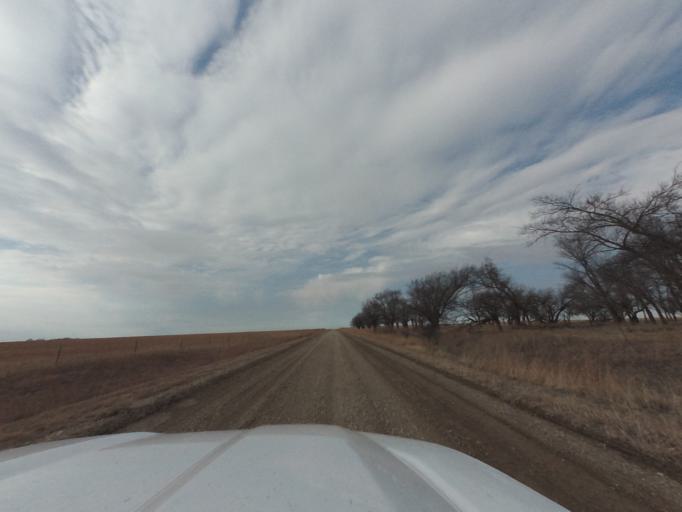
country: US
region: Kansas
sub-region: Chase County
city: Cottonwood Falls
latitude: 38.2172
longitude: -96.7086
